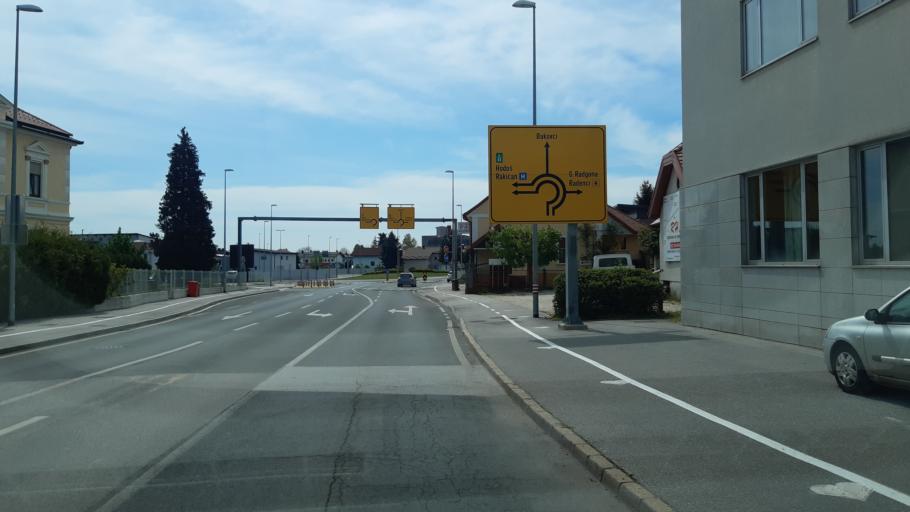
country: SI
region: Murska Sobota
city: Murska Sobota
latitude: 46.6578
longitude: 16.1691
